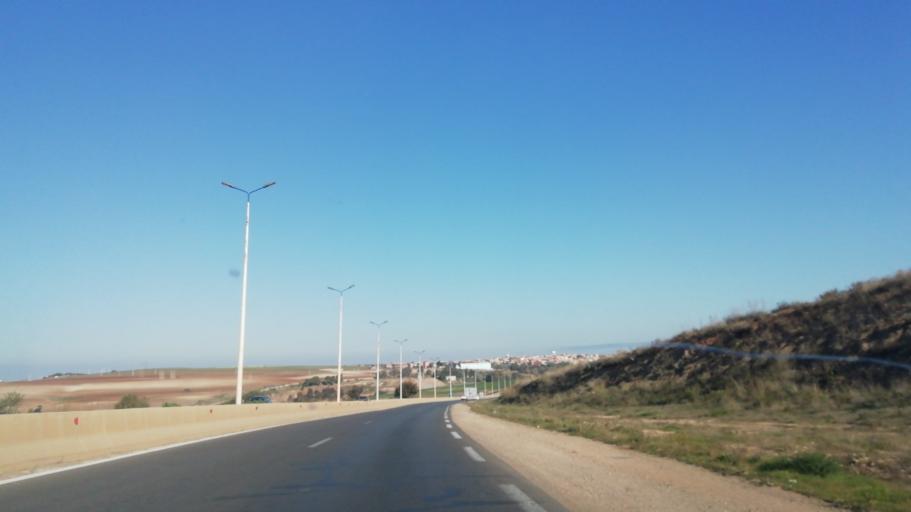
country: DZ
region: Ain Temouchent
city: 'Ain Temouchent
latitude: 35.2983
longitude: -1.1738
